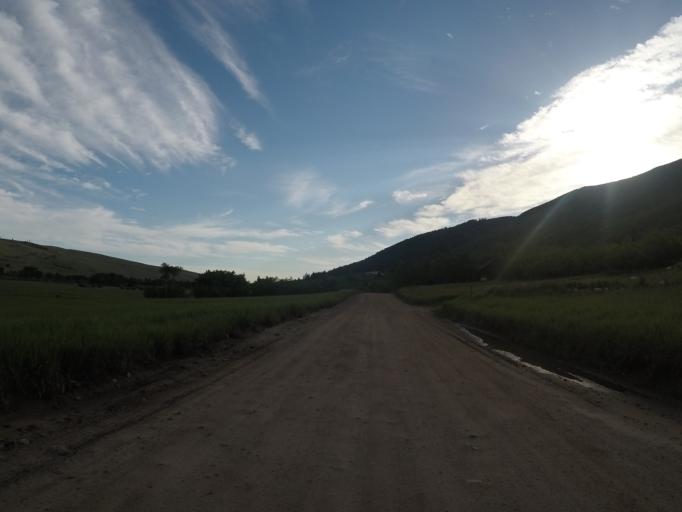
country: US
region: Montana
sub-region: Stillwater County
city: Absarokee
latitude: 45.2715
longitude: -109.5543
